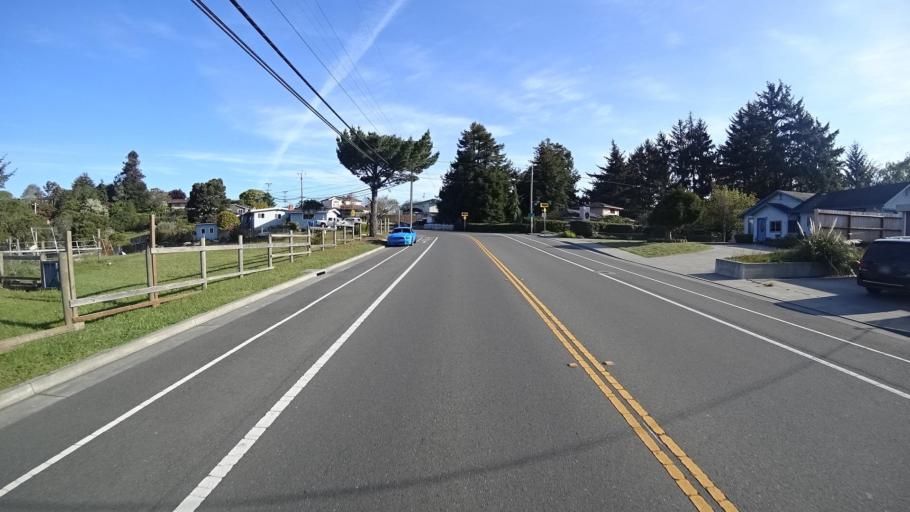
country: US
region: California
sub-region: Humboldt County
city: Bayview
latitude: 40.7729
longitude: -124.1740
